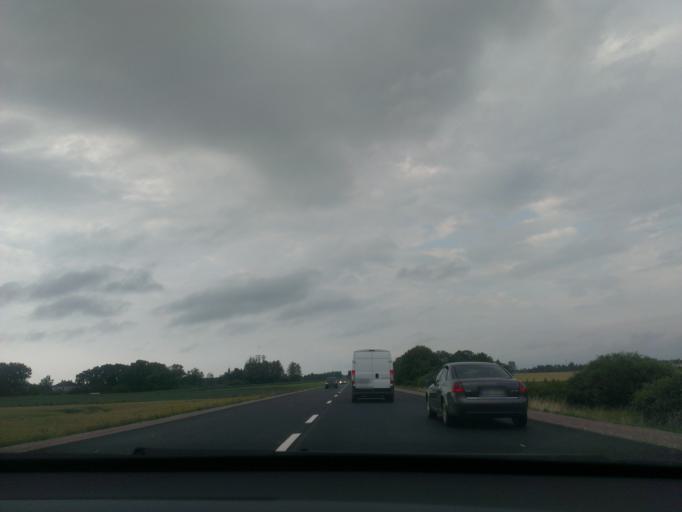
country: LV
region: Lecava
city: Iecava
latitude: 56.6162
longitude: 24.2165
